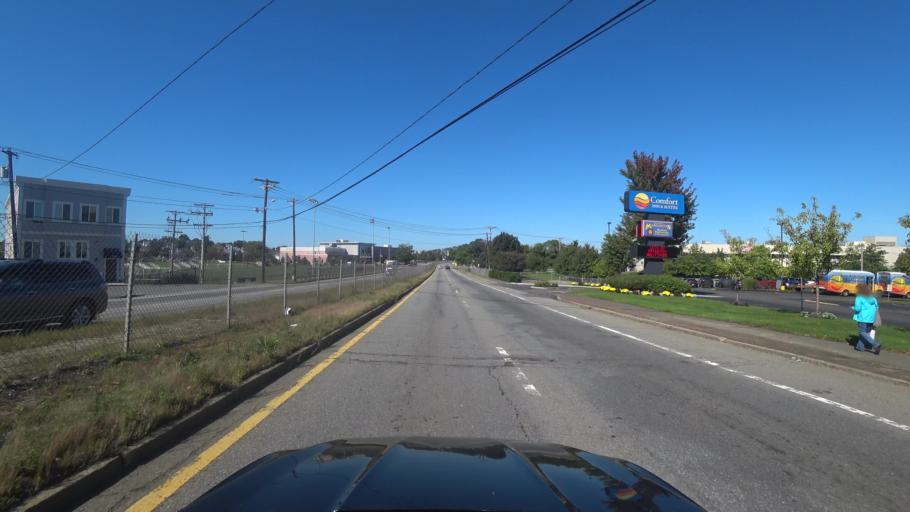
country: US
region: Massachusetts
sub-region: Suffolk County
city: Revere
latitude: 42.4111
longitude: -71.0022
